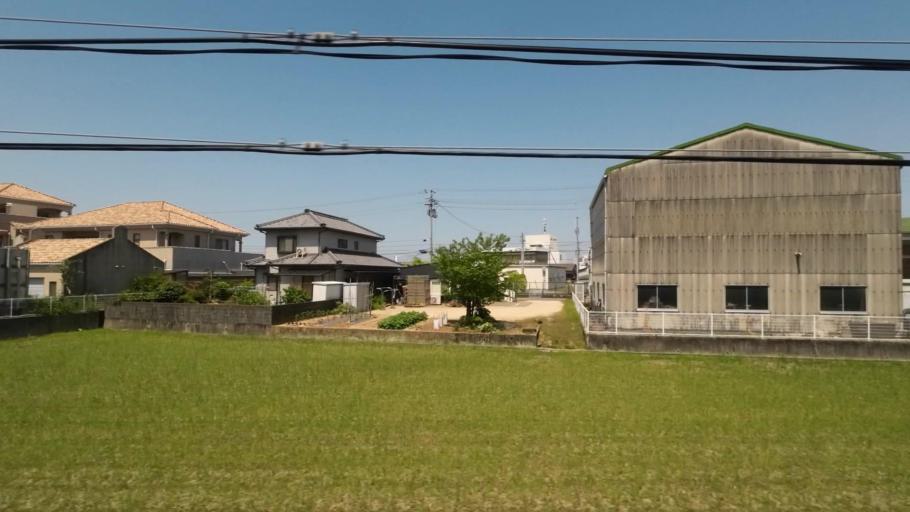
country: JP
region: Ehime
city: Hojo
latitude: 34.0374
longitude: 132.8462
